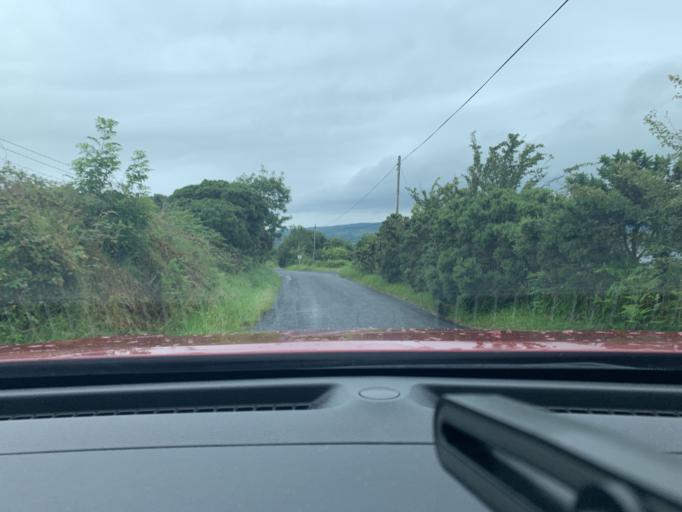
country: GB
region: Northern Ireland
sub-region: Fermanagh District
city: Enniskillen
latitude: 54.2744
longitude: -7.8569
